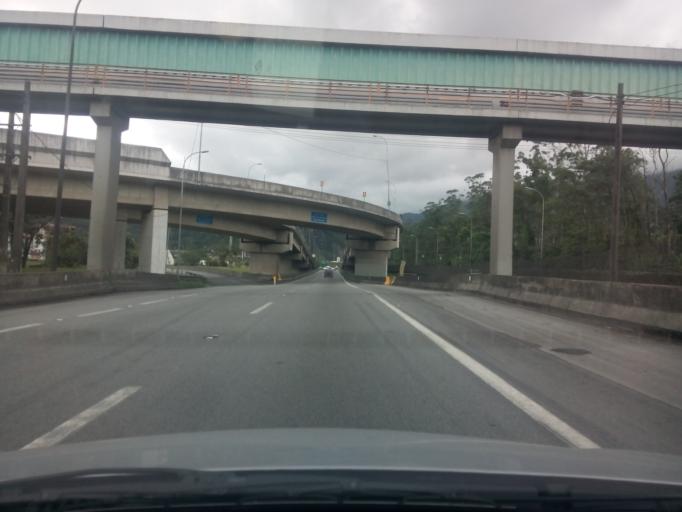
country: BR
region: Sao Paulo
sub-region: Cubatao
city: Cubatao
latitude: -23.8865
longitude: -46.4317
